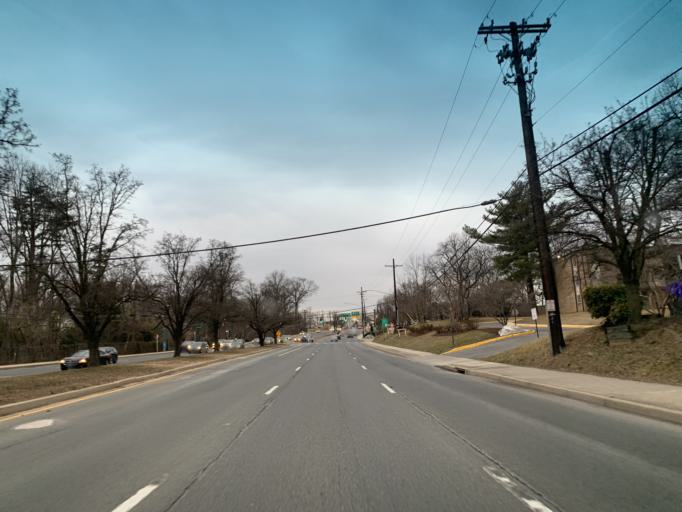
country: US
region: Maryland
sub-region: Montgomery County
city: Glenmont
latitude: 39.0614
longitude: -77.0438
